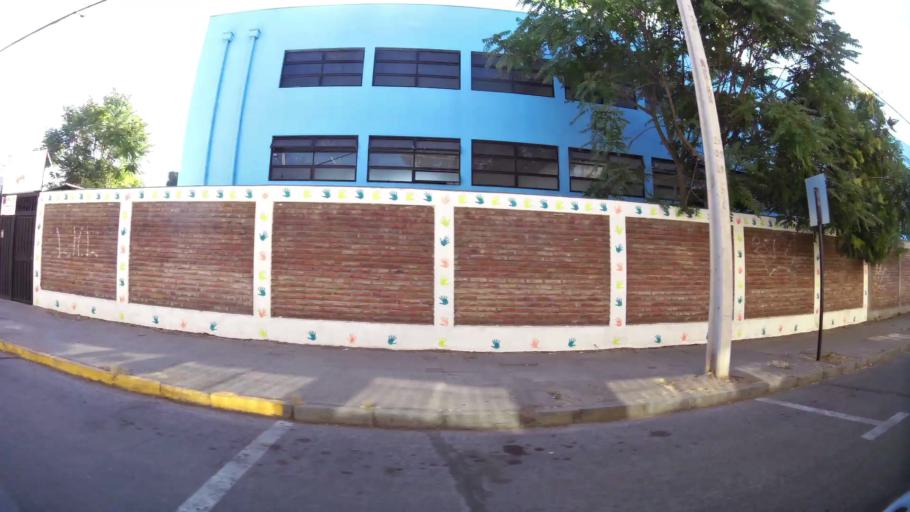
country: CL
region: O'Higgins
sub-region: Provincia de Colchagua
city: Chimbarongo
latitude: -34.5828
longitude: -70.9894
